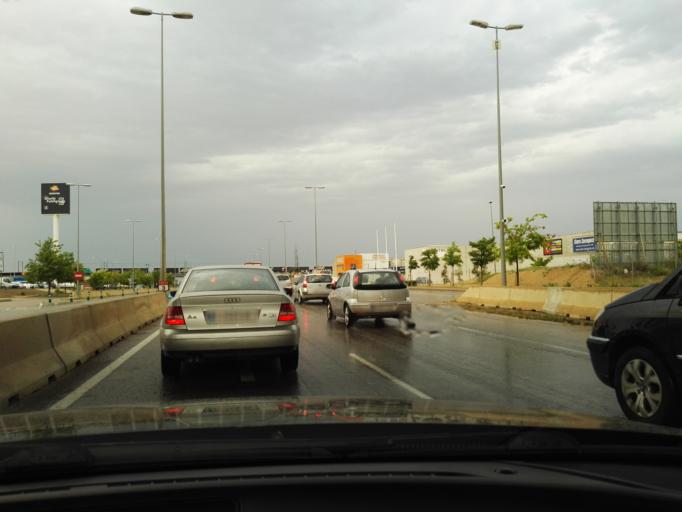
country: ES
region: Aragon
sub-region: Provincia de Zaragoza
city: Montecanal
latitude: 41.6343
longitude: -0.9894
